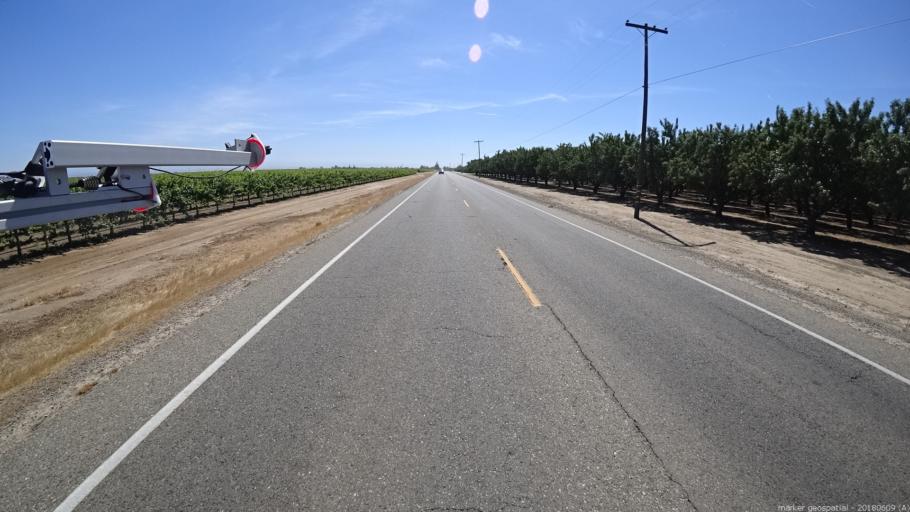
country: US
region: California
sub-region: Madera County
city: Madera
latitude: 36.9529
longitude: -120.1439
